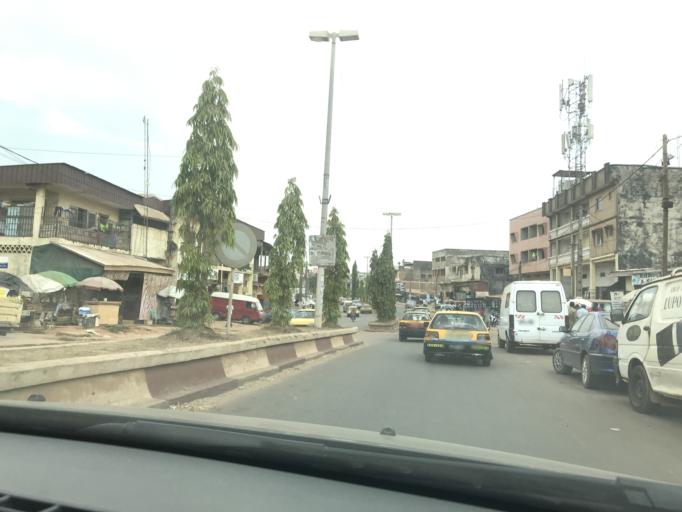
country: CM
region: Centre
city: Yaounde
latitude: 3.8874
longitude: 11.5267
